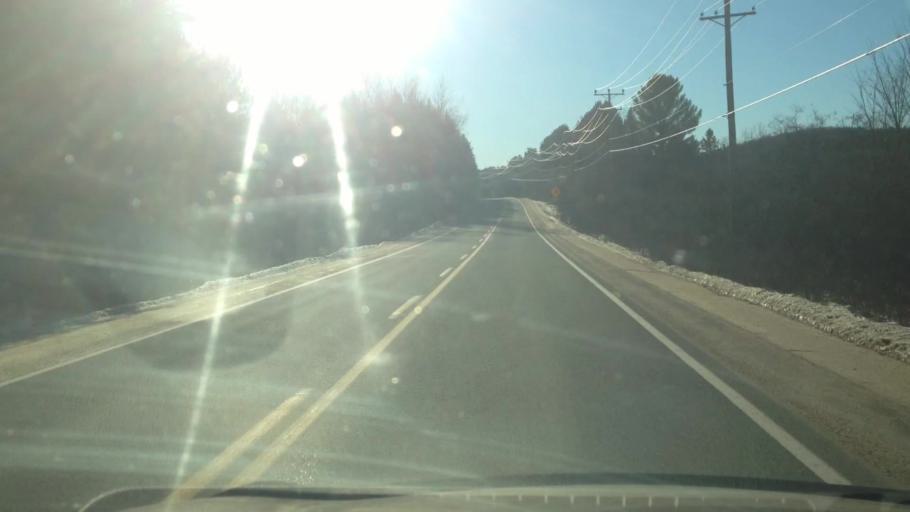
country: CA
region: Quebec
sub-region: Laurentides
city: Mont-Tremblant
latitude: 46.0044
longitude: -74.6194
